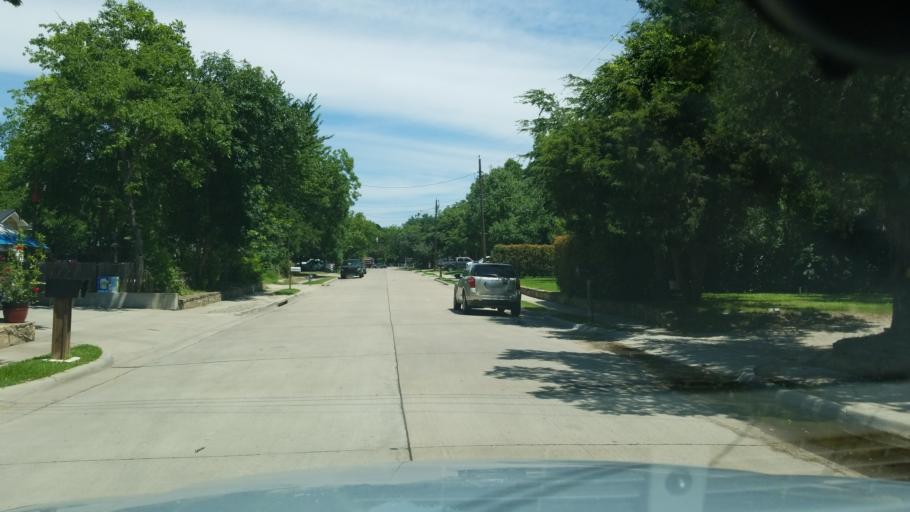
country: US
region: Texas
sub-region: Dallas County
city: Irving
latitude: 32.8183
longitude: -96.9360
